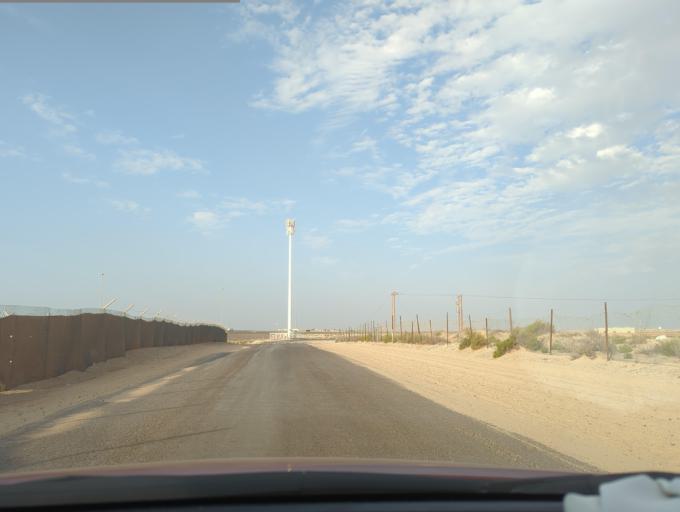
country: AE
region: Dubai
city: Dubai
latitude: 24.7204
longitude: 54.8674
